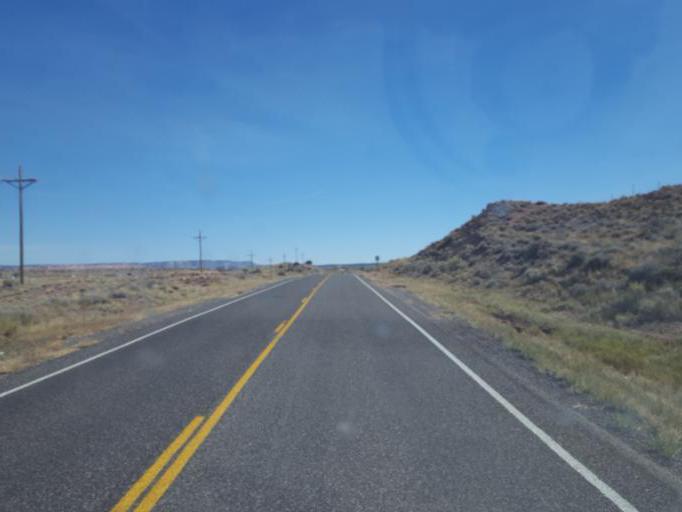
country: US
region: New Mexico
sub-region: McKinley County
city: Church Rock
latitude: 35.5095
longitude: -108.5326
